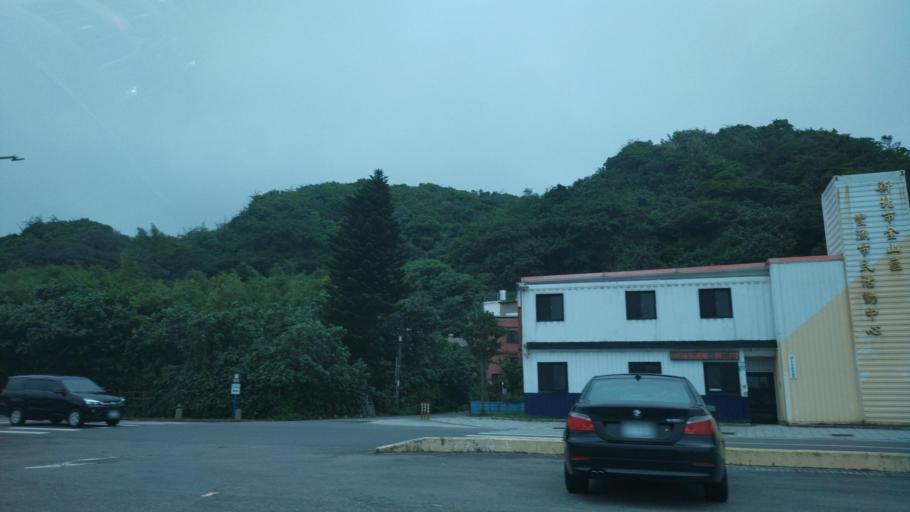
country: TW
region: Taiwan
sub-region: Keelung
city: Keelung
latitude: 25.2227
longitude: 121.6469
